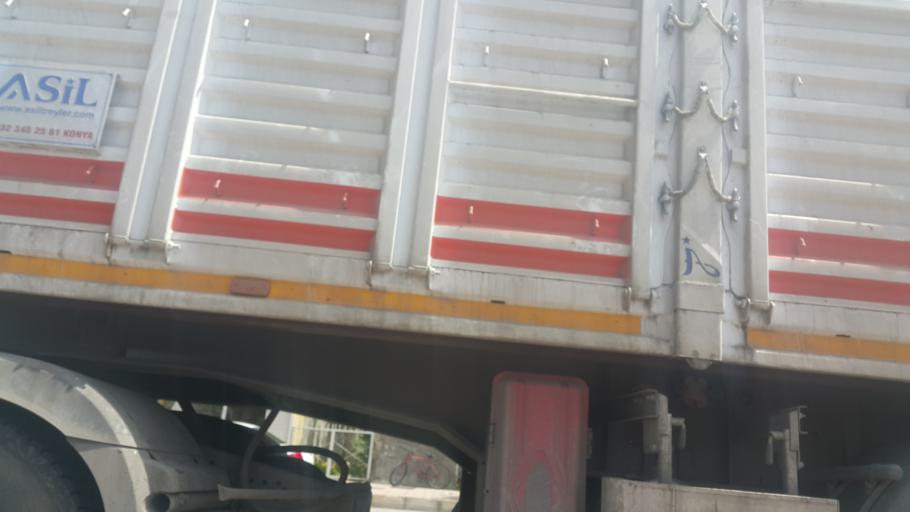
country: TR
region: Hatay
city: Denizciler
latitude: 36.6710
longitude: 36.2133
